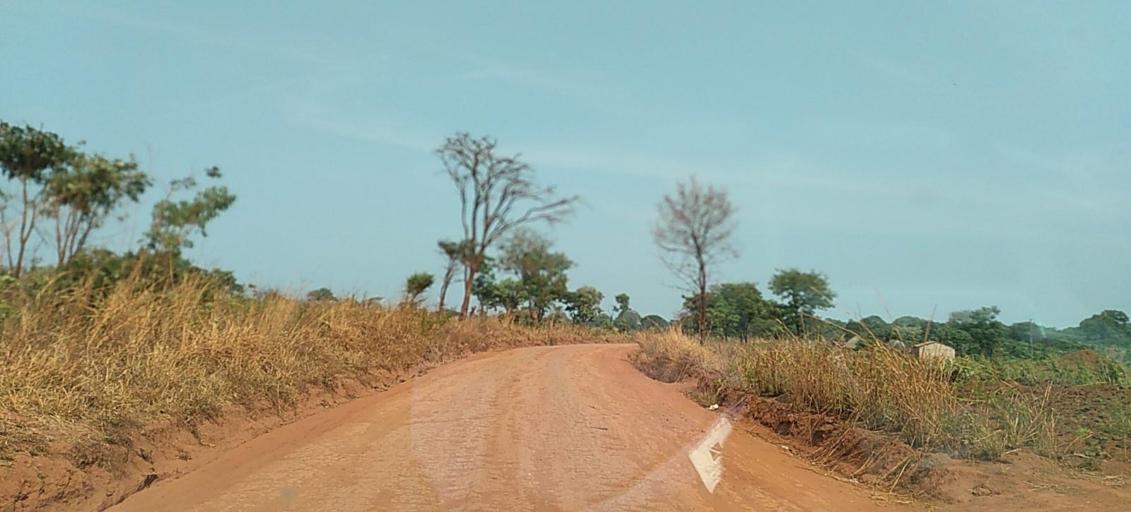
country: ZM
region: Copperbelt
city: Chililabombwe
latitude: -12.3425
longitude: 27.7013
